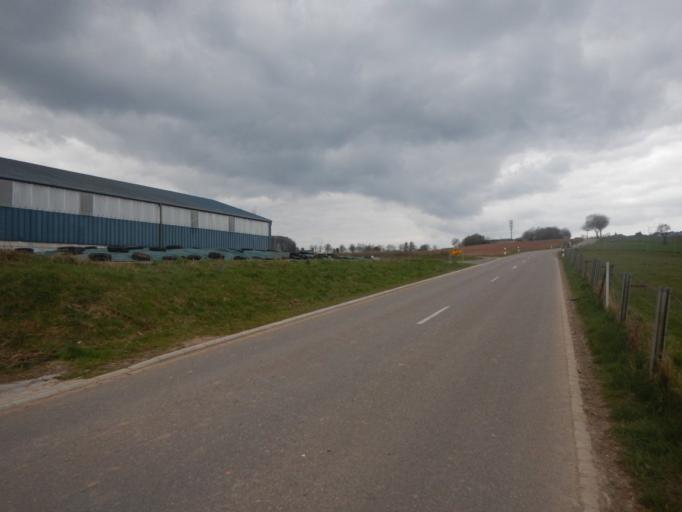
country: LU
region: Diekirch
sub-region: Canton de Redange
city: Ell
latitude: 49.7902
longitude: 5.8352
